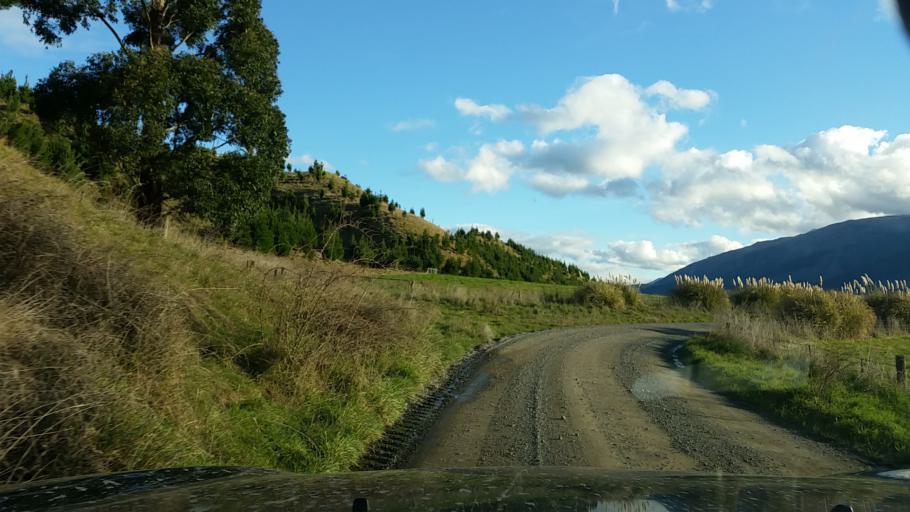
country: NZ
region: Marlborough
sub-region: Marlborough District
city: Blenheim
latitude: -41.7233
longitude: 173.9094
